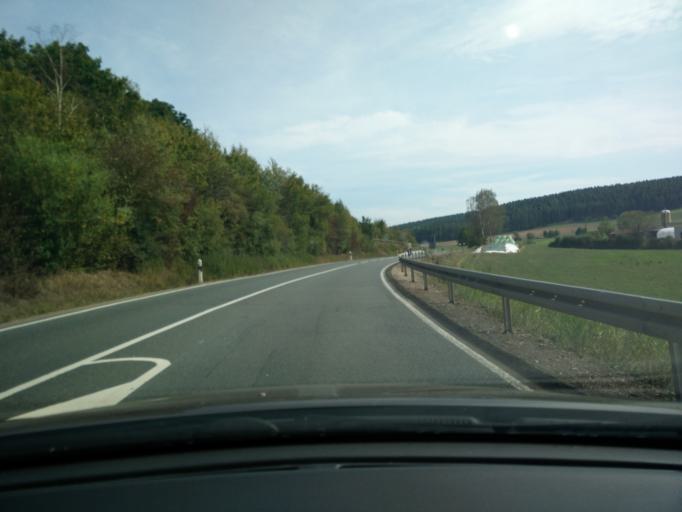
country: DE
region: Bavaria
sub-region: Regierungsbezirk Mittelfranken
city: Wilhelmsdorf
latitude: 49.5592
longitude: 10.7450
